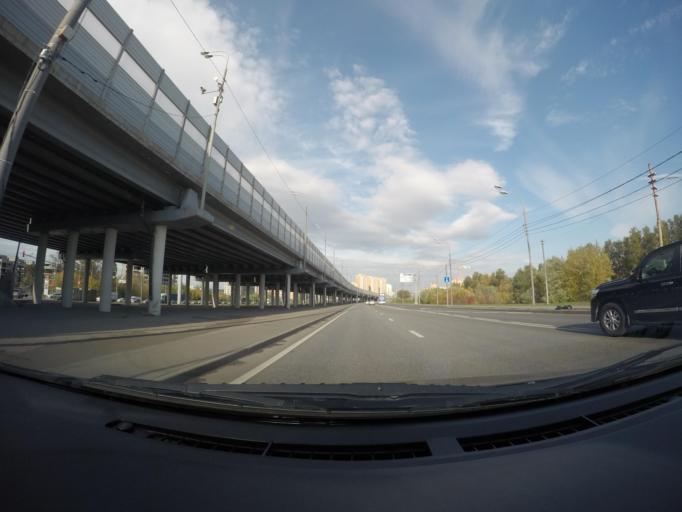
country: RU
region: Moscow
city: Vagonoremont
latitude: 55.9167
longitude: 37.5447
